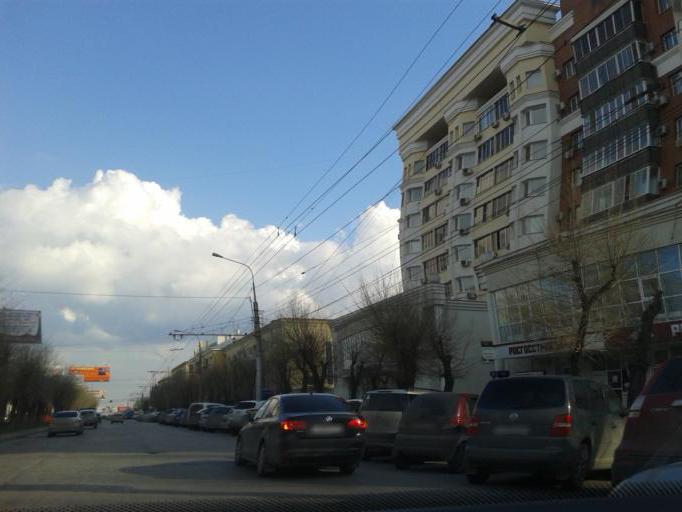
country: RU
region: Volgograd
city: Volgograd
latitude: 48.7179
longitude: 44.5082
